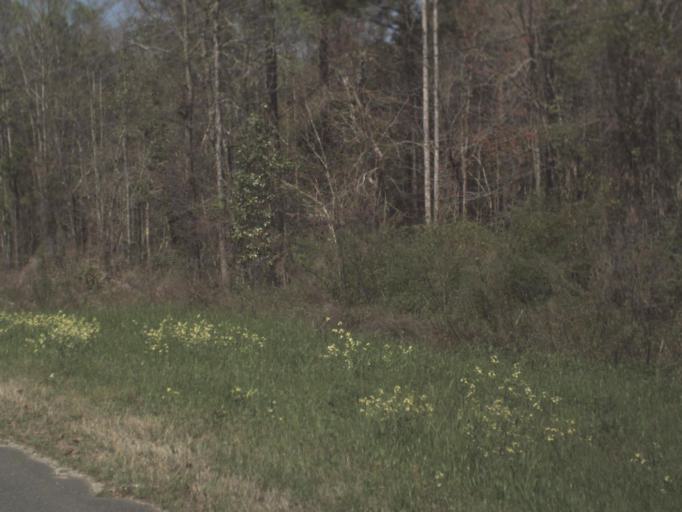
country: US
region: Florida
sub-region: Jackson County
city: Graceville
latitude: 30.9642
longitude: -85.5357
